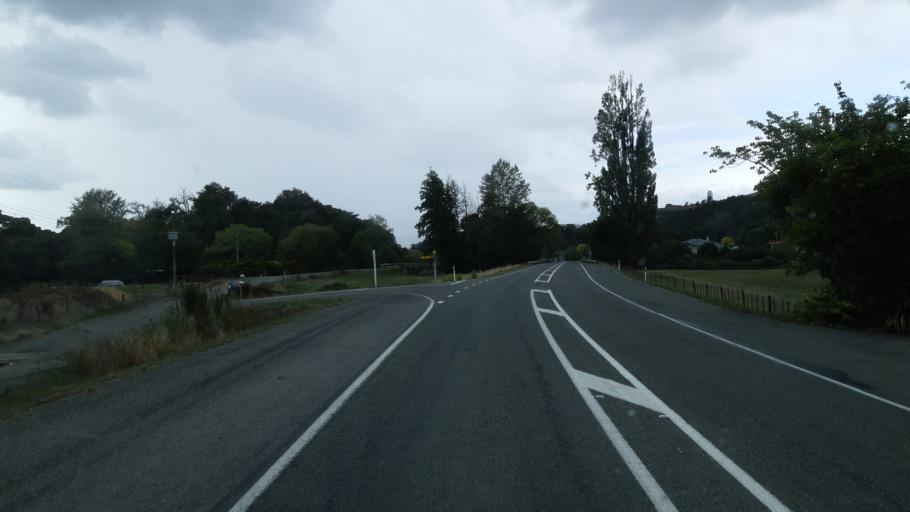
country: NZ
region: Tasman
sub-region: Tasman District
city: Wakefield
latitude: -41.4083
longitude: 173.0314
